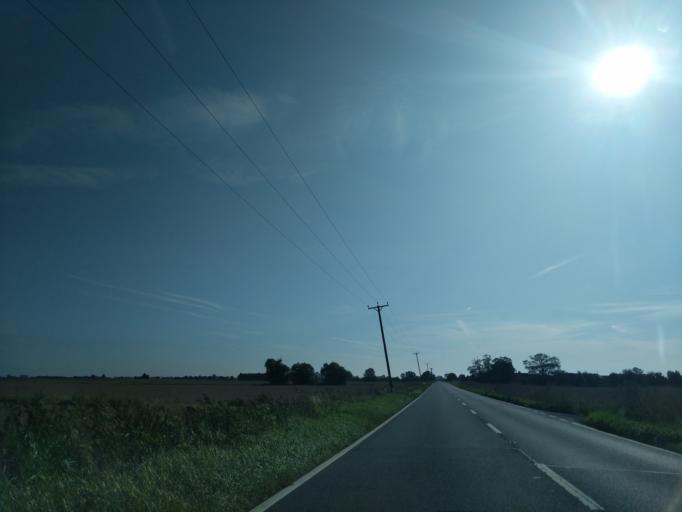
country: GB
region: England
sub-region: Lincolnshire
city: Bourne
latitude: 52.7720
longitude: -0.3145
